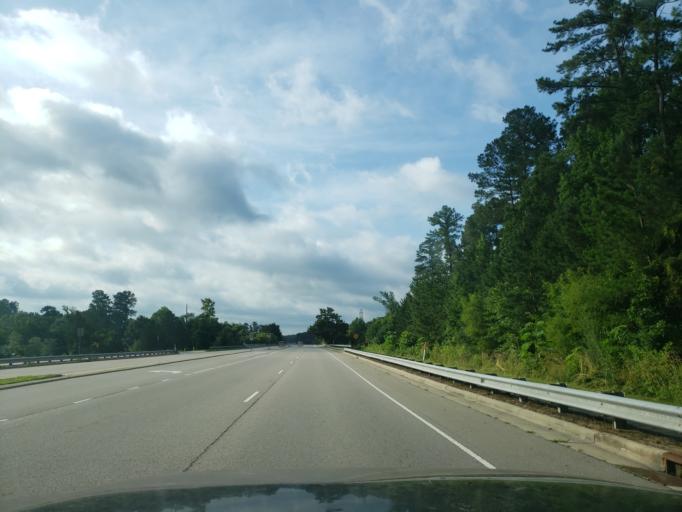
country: US
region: North Carolina
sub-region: Durham County
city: Durham
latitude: 35.9531
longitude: -78.9289
